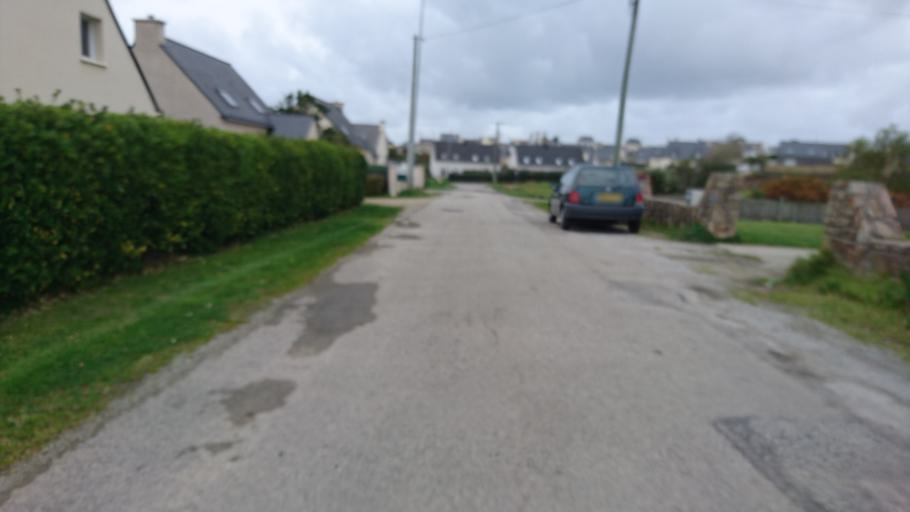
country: FR
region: Brittany
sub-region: Departement du Finistere
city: Lampaul-Plouarzel
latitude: 48.4454
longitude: -4.7662
